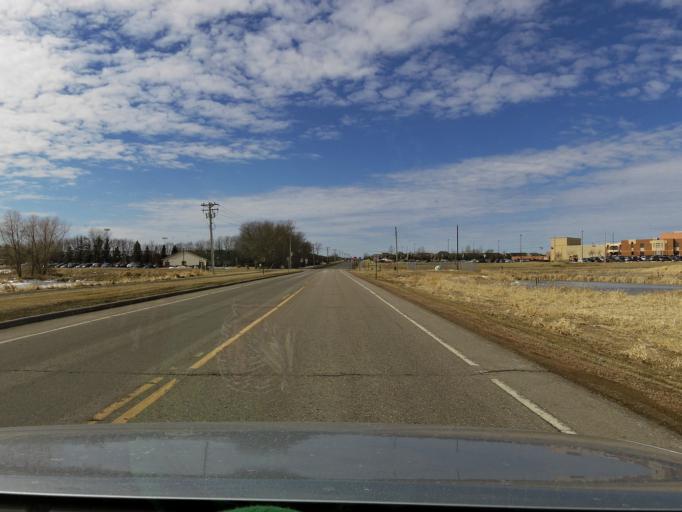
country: US
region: Minnesota
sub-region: Le Sueur County
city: New Prague
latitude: 44.5580
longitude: -93.5725
